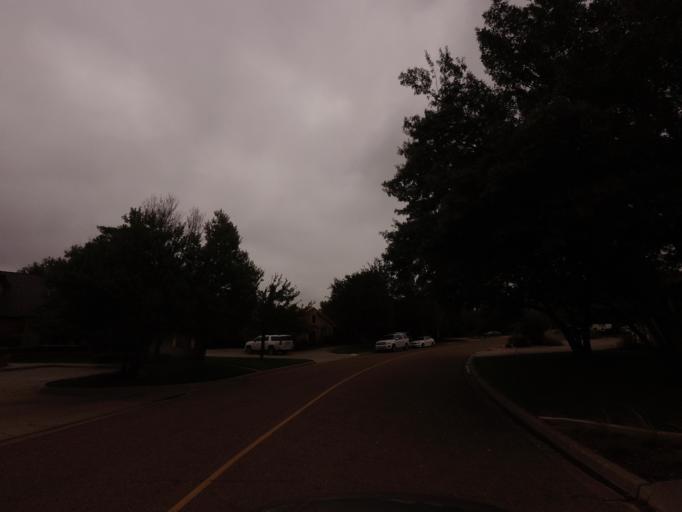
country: US
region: New Mexico
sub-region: Curry County
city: Clovis
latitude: 34.4296
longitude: -103.1824
